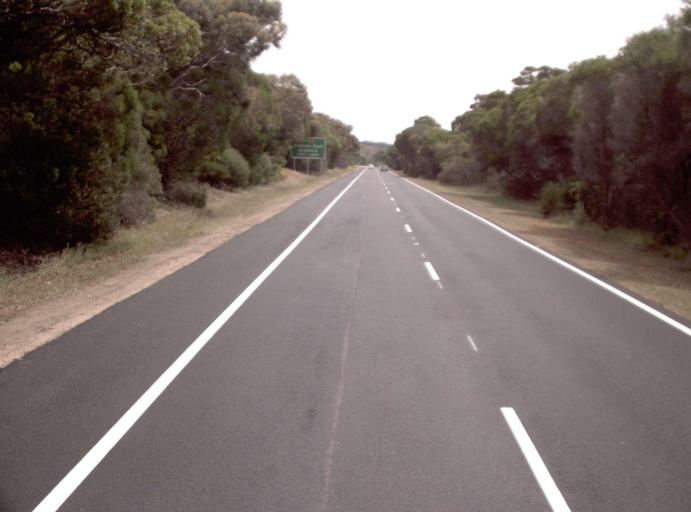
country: AU
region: Victoria
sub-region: Mornington Peninsula
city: Dromana
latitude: -38.3388
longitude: 144.9682
